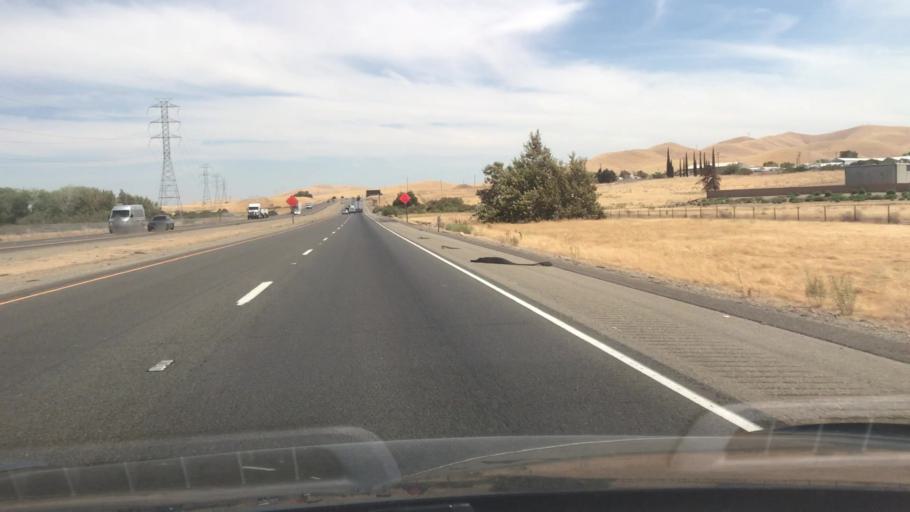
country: US
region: California
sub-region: Merced County
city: Gustine
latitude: 37.0635
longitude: -121.0645
